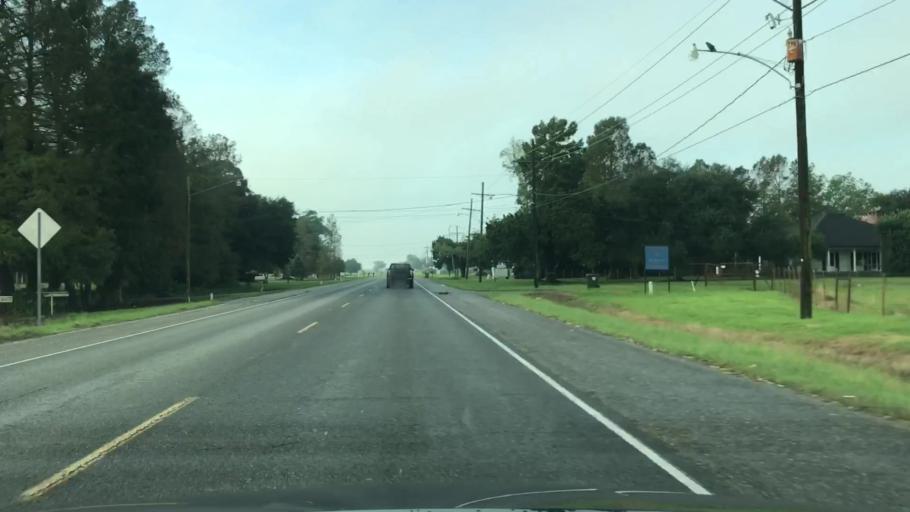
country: US
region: Louisiana
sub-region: Terrebonne Parish
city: Gray
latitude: 29.6712
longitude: -90.8163
